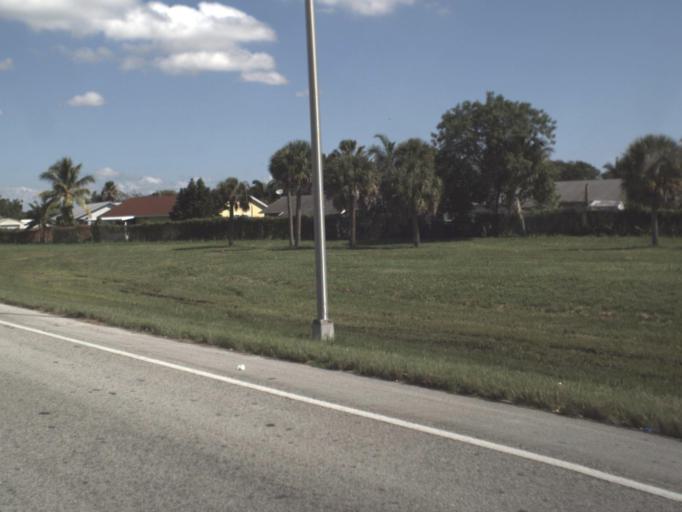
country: US
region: Florida
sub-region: Miami-Dade County
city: Naranja
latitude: 25.5053
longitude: -80.4166
